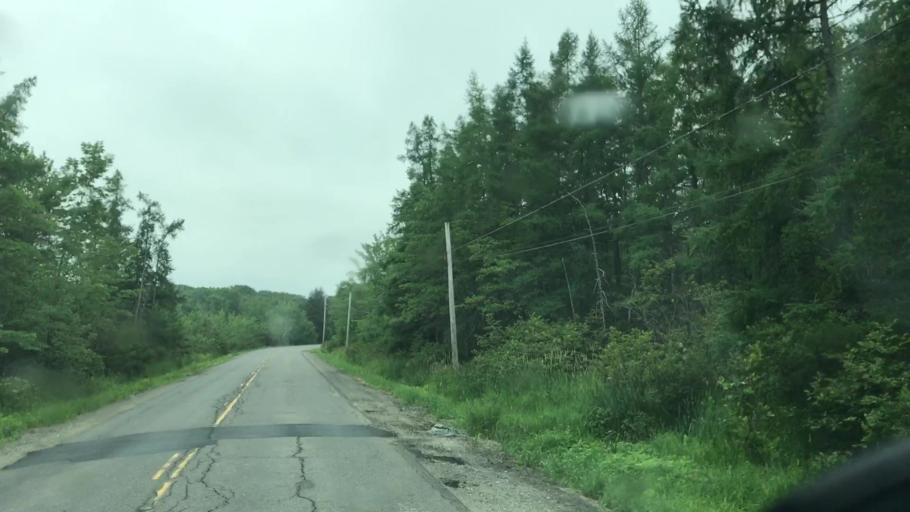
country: US
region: Maine
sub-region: Penobscot County
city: Veazie
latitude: 44.8687
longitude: -68.7160
